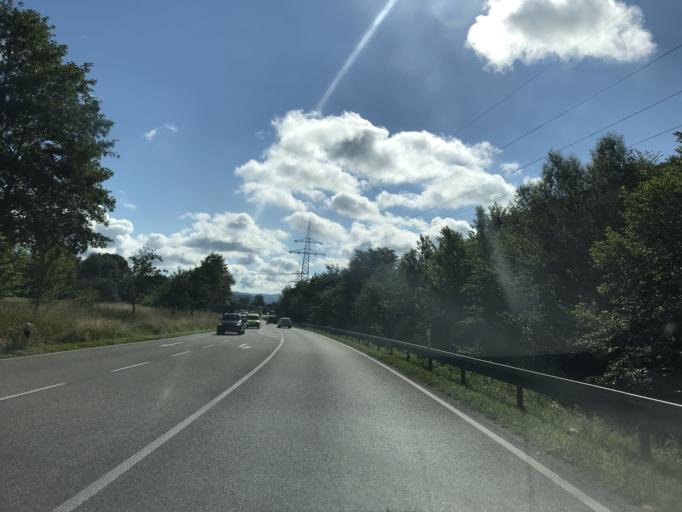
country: DE
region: Baden-Wuerttemberg
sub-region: Freiburg Region
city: Steinen
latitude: 47.6380
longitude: 7.7126
